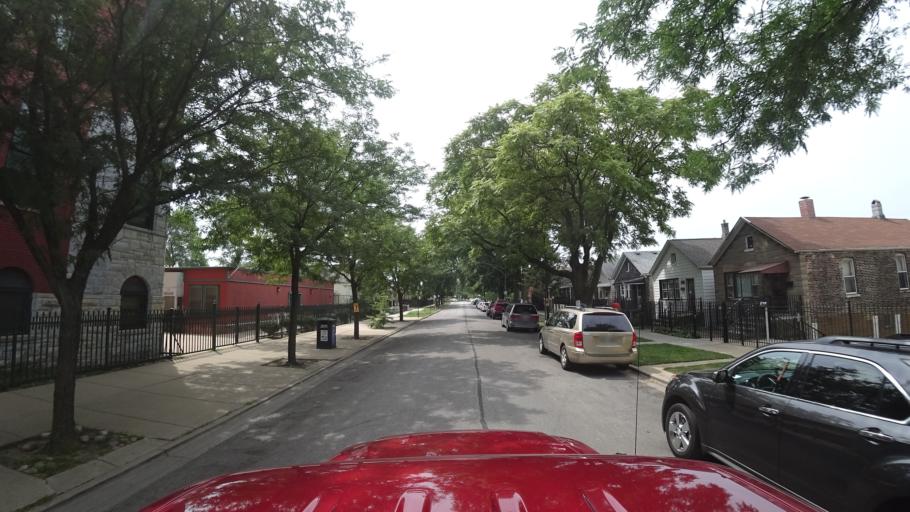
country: US
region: Illinois
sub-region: Cook County
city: Chicago
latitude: 41.8318
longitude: -87.6814
